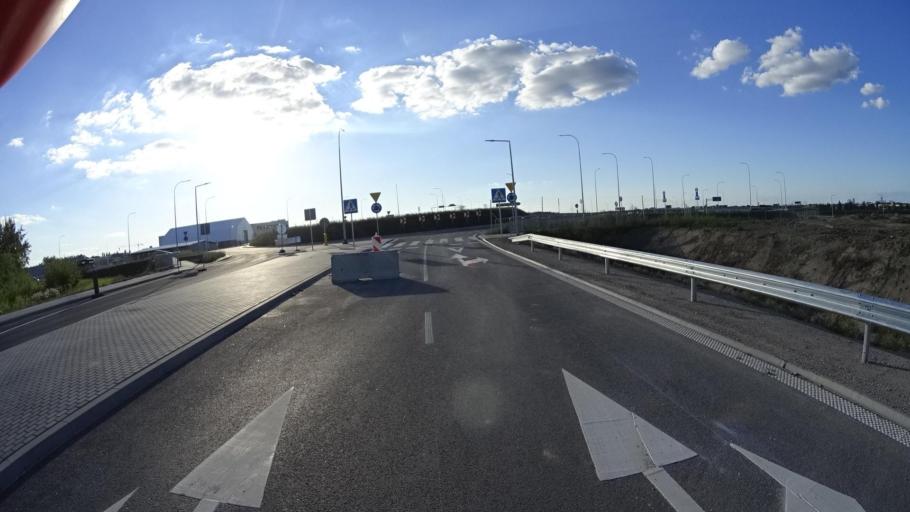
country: PL
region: Masovian Voivodeship
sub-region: Powiat piaseczynski
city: Mysiadlo
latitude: 52.1153
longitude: 20.9888
